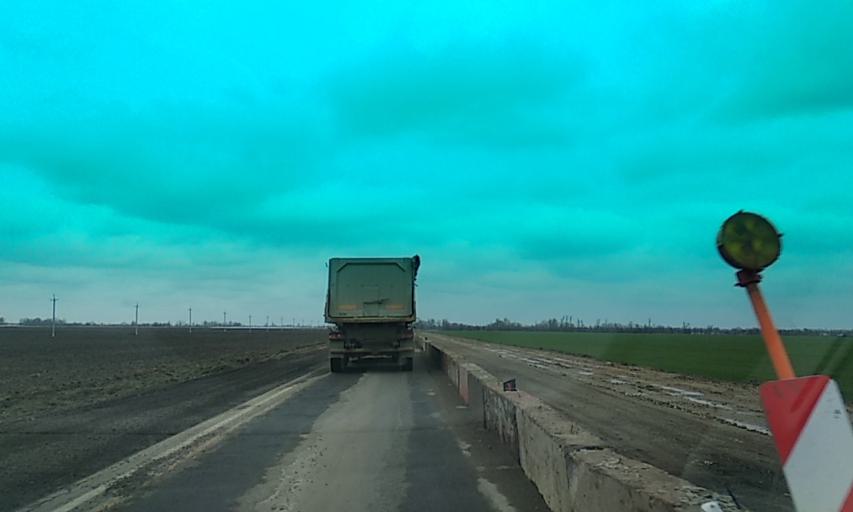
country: RU
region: Adygeya
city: Beloye
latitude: 45.0229
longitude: 39.6879
